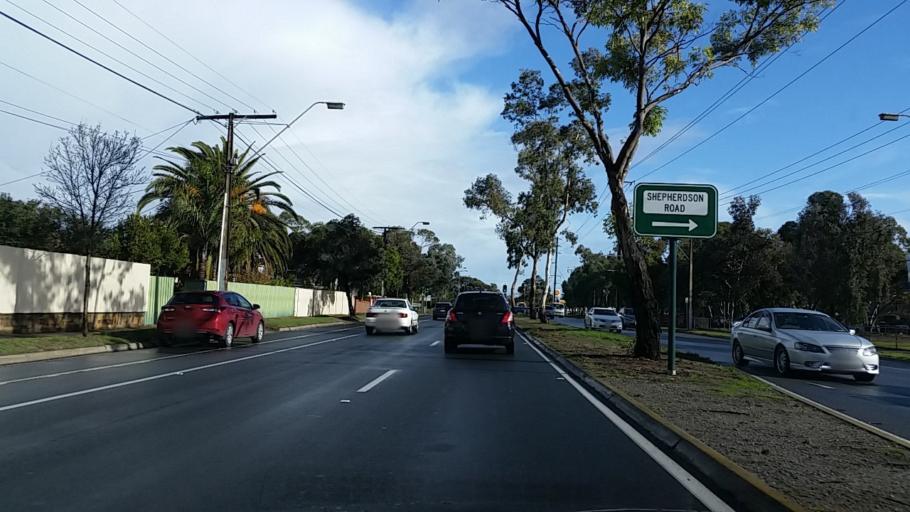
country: AU
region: South Australia
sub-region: Salisbury
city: Salisbury
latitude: -34.7865
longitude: 138.6199
